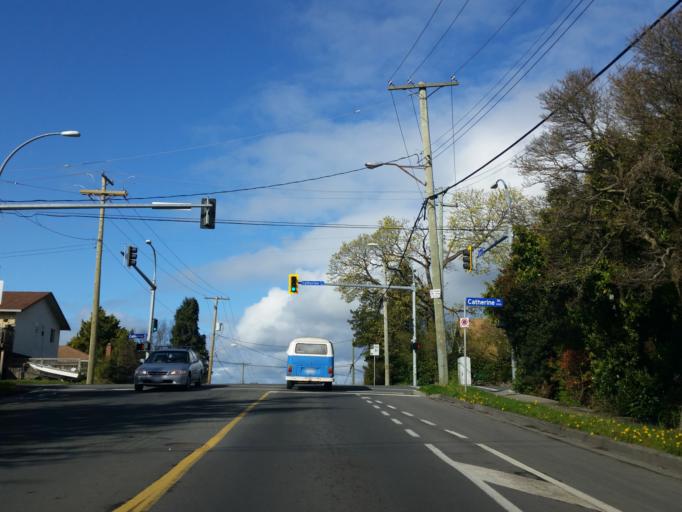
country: CA
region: British Columbia
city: Victoria
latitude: 48.4356
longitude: -123.3843
